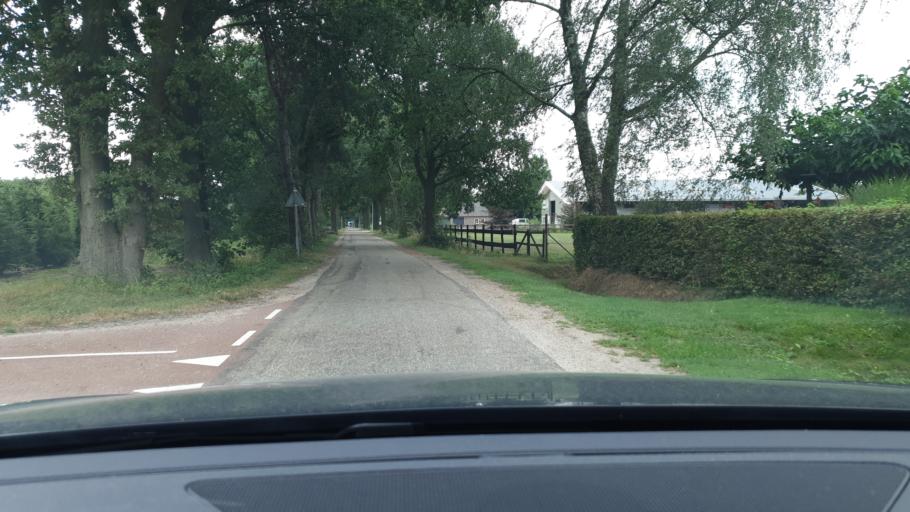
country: NL
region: North Brabant
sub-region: Gemeente Best
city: Best
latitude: 51.5018
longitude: 5.3626
